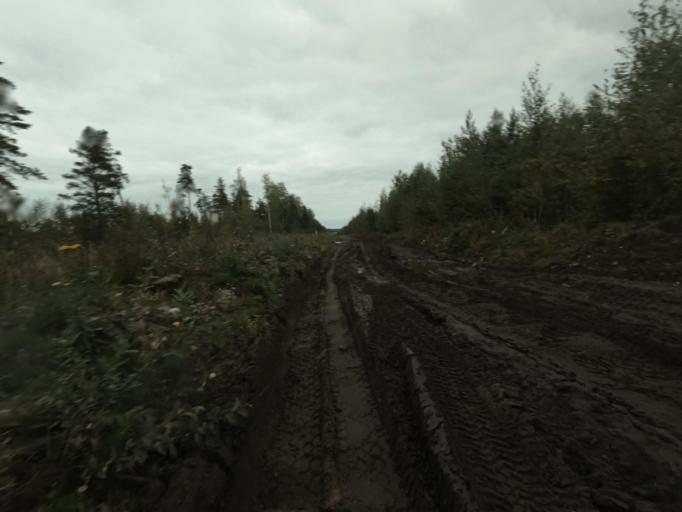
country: RU
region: St.-Petersburg
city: Sapernyy
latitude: 59.7598
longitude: 30.7151
